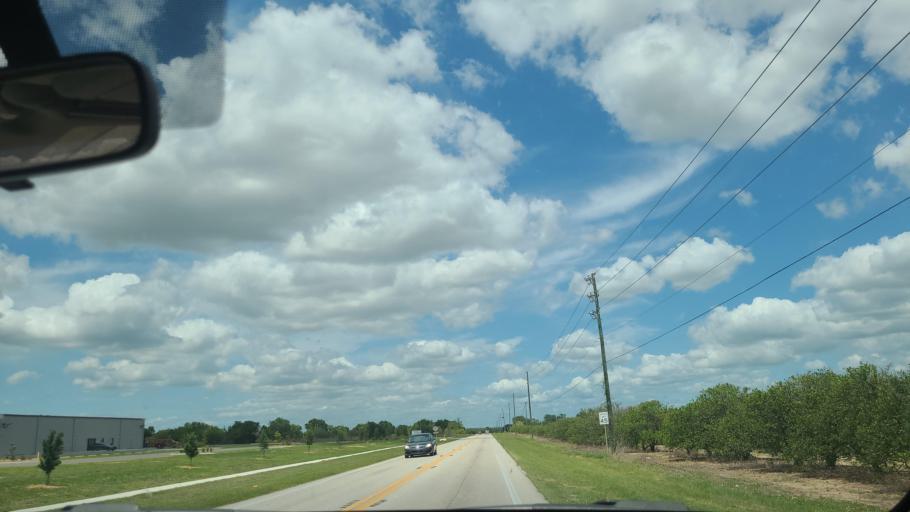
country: US
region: Florida
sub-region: Polk County
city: Lake Wales
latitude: 27.9018
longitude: -81.5560
